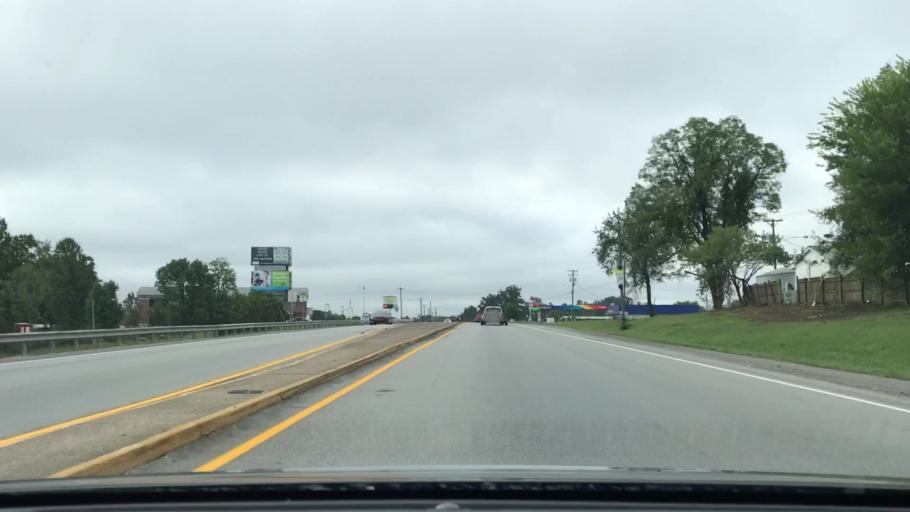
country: US
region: Kentucky
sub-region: Russell County
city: Russell Springs
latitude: 37.0378
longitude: -85.0748
